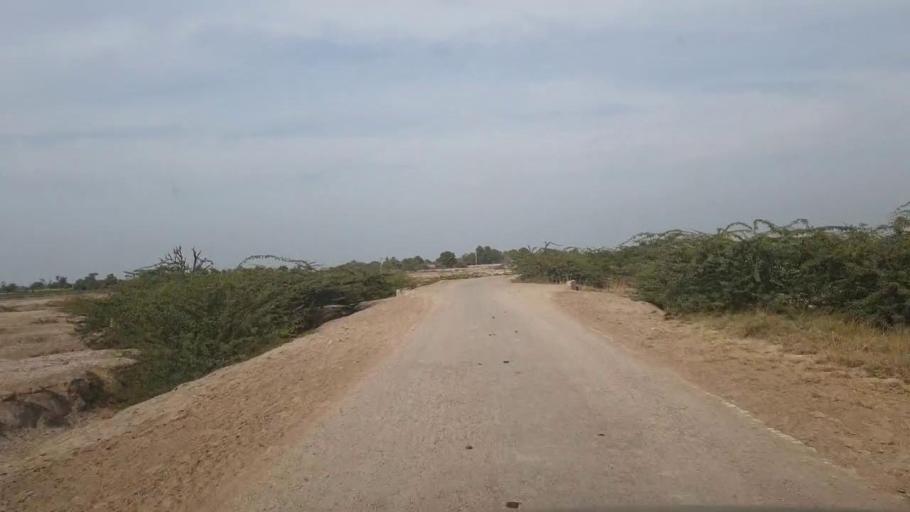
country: PK
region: Sindh
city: Shahpur Chakar
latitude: 26.1043
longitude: 68.5047
